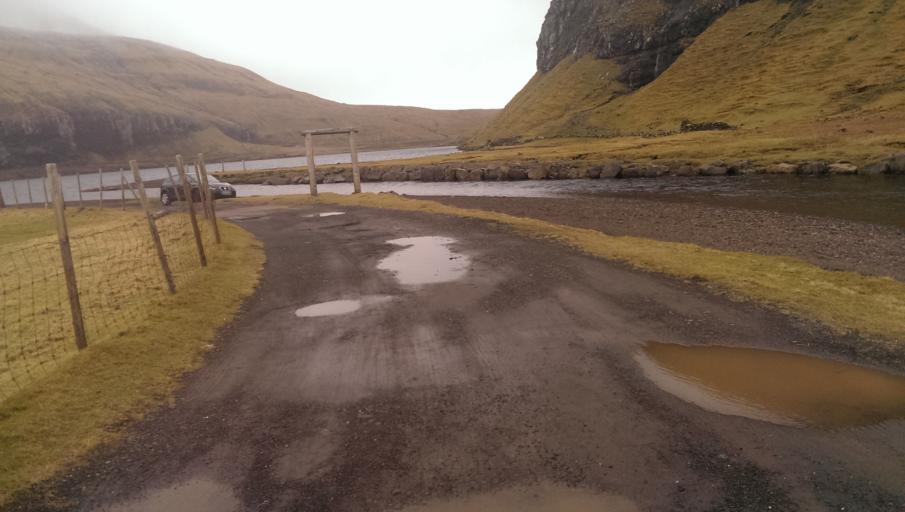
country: FO
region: Streymoy
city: Kollafjordhur
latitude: 62.1313
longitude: -7.0240
